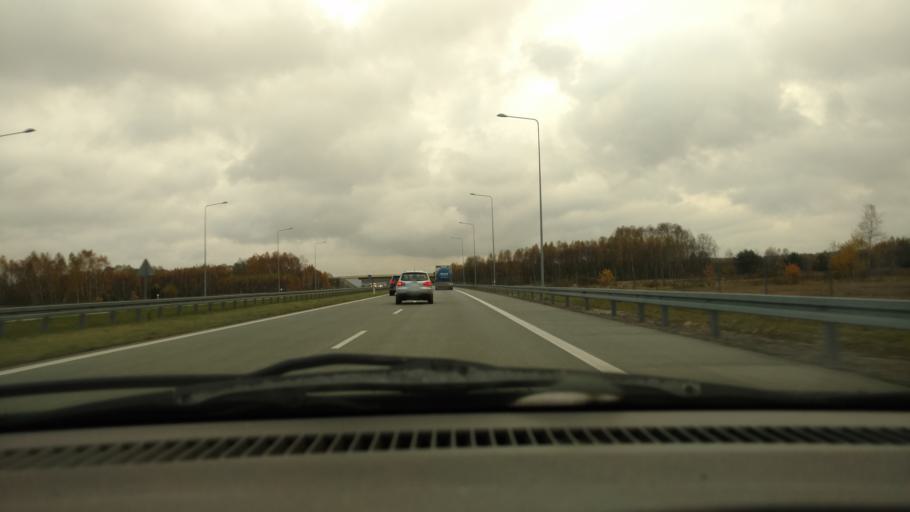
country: PL
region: Lodz Voivodeship
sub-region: Powiat lodzki wschodni
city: Rzgow
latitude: 51.6330
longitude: 19.4462
